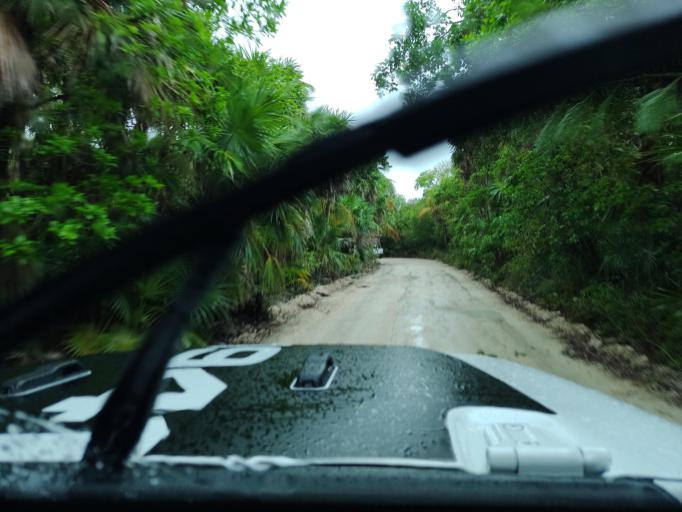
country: MX
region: Quintana Roo
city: Tulum
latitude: 19.9761
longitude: -87.4686
